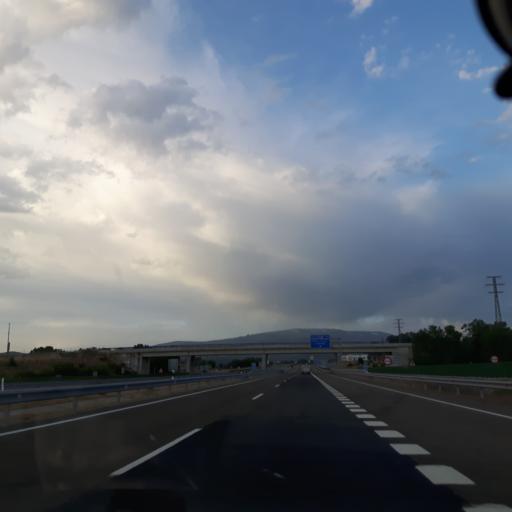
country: ES
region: Castille and Leon
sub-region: Provincia de Salamanca
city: Nava de Bejar
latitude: 40.4901
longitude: -5.6766
